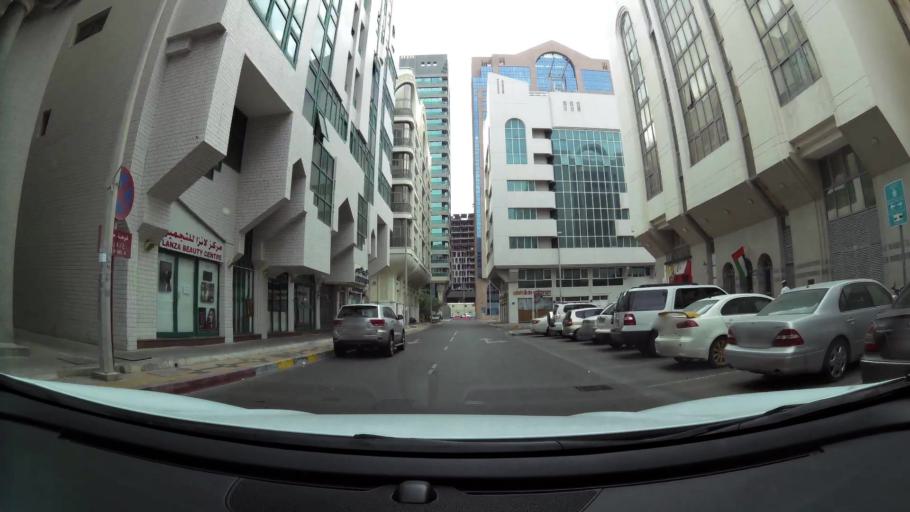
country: AE
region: Abu Dhabi
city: Abu Dhabi
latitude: 24.4737
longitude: 54.3520
